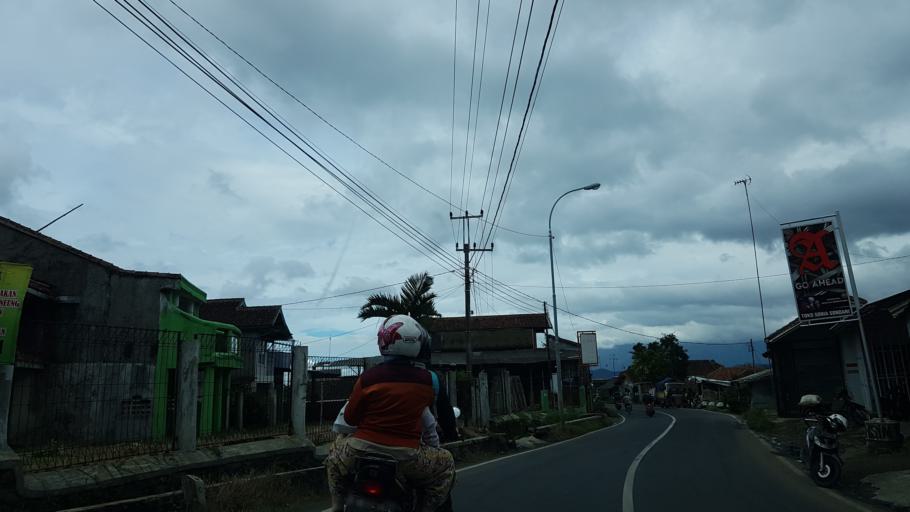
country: ID
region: West Java
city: Banjar
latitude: -7.1187
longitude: 107.4330
